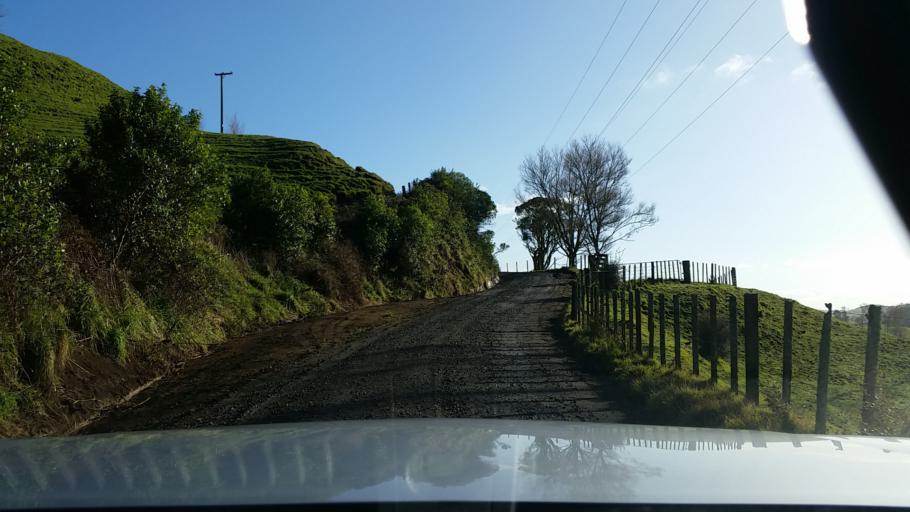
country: NZ
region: Taranaki
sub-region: South Taranaki District
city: Eltham
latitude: -39.4563
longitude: 174.3692
